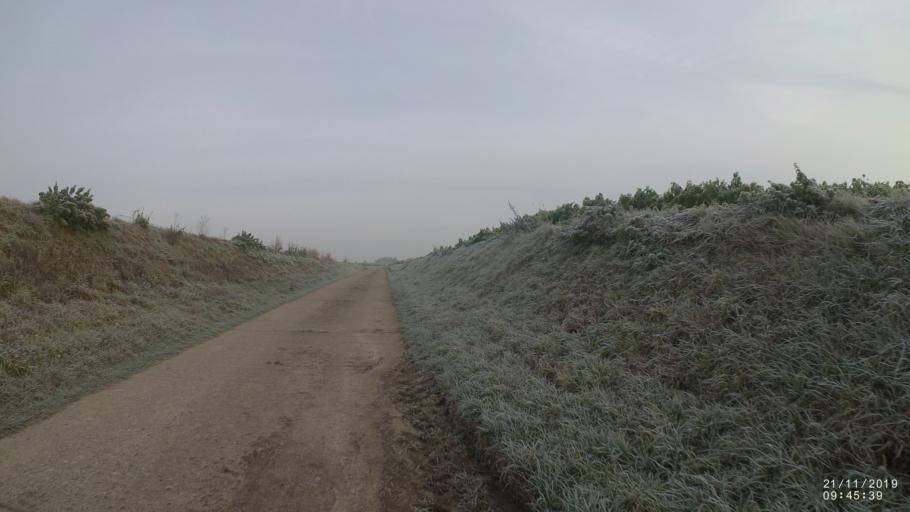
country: BE
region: Flanders
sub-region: Provincie Vlaams-Brabant
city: Tienen
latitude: 50.7900
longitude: 5.0022
